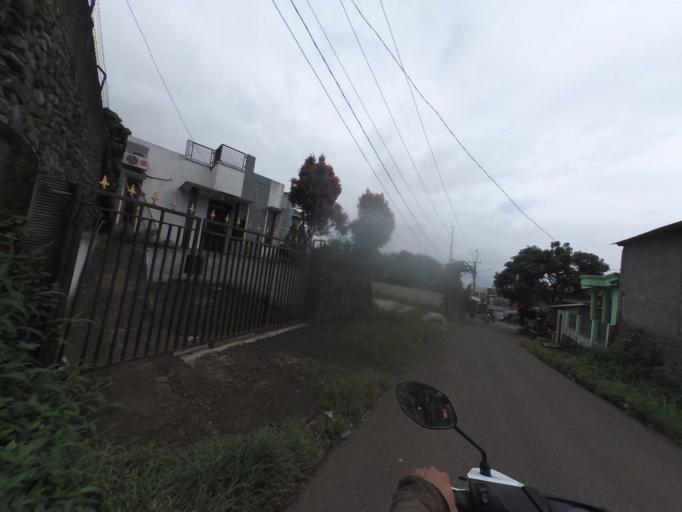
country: ID
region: West Java
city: Bogor
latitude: -6.6231
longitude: 106.7460
